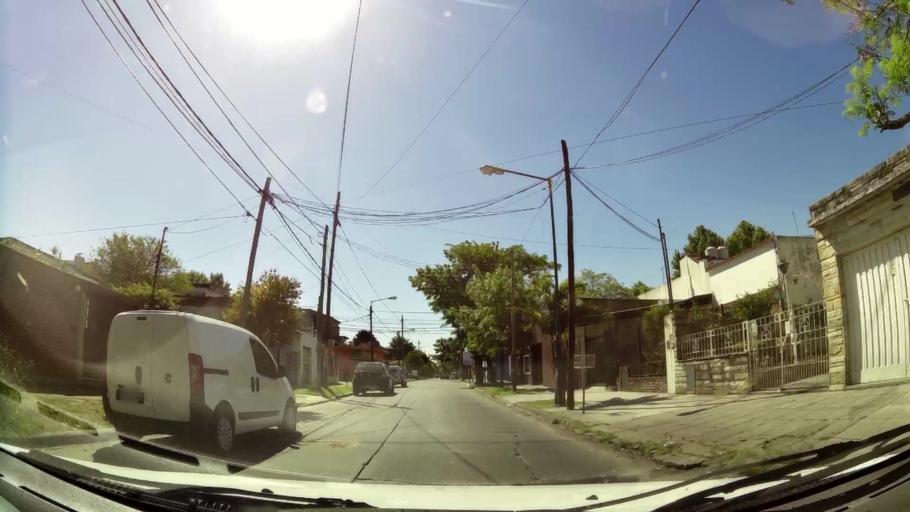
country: AR
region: Buenos Aires
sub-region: Partido de General San Martin
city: General San Martin
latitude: -34.5454
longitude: -58.5693
